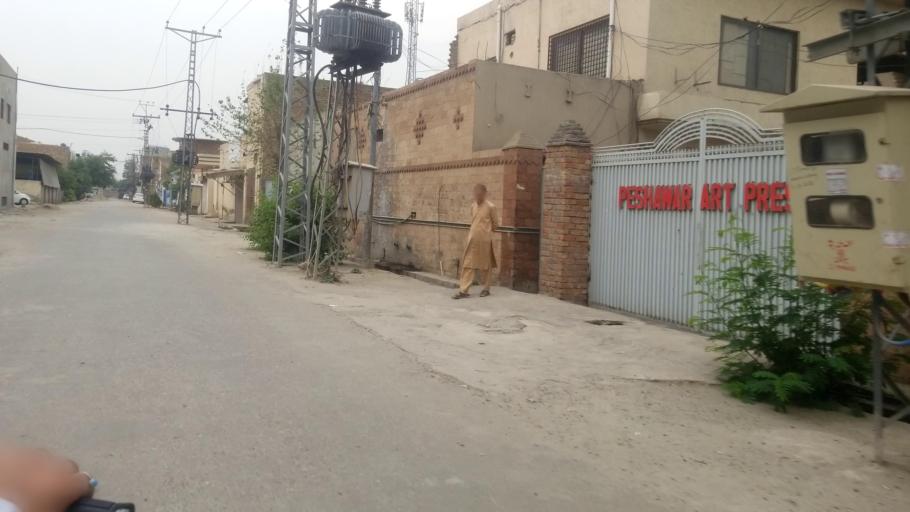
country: PK
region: Khyber Pakhtunkhwa
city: Peshawar
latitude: 33.9821
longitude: 71.5581
